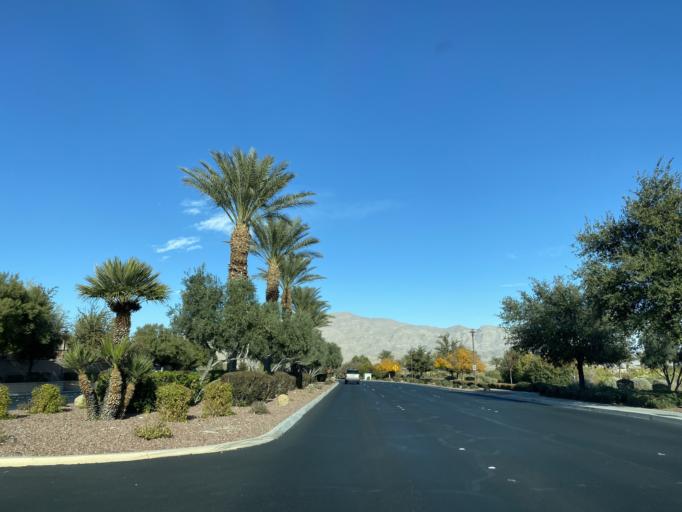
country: US
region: Nevada
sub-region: Clark County
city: North Las Vegas
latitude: 36.3125
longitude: -115.2596
